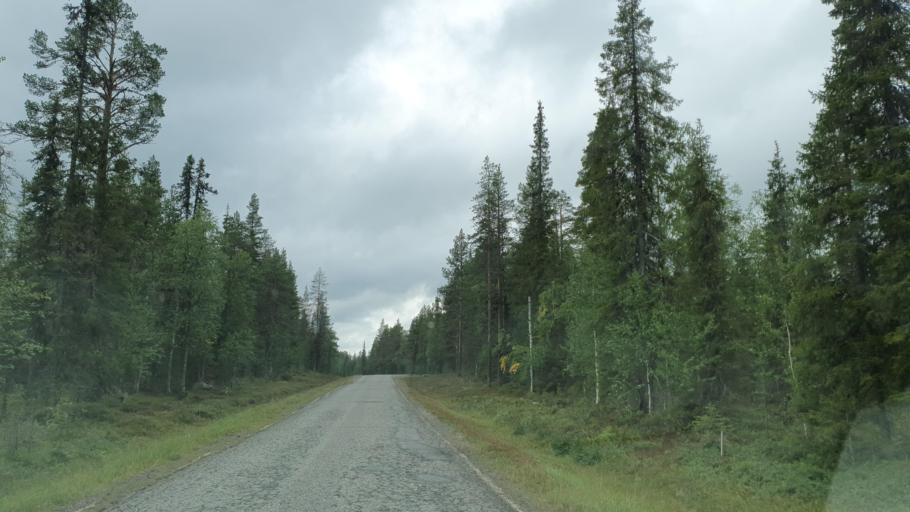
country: FI
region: Lapland
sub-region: Tunturi-Lappi
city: Muonio
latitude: 67.7338
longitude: 24.2688
